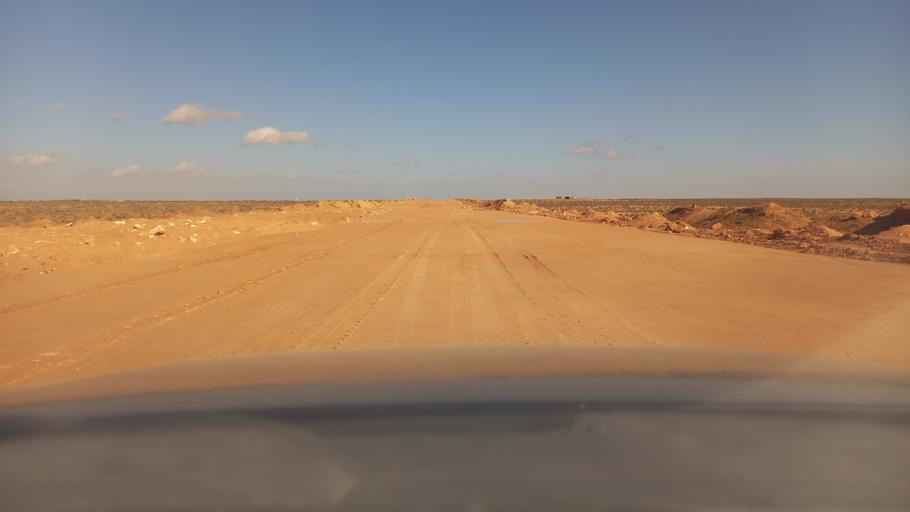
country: TN
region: Madanin
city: Medenine
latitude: 33.2409
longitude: 10.5560
